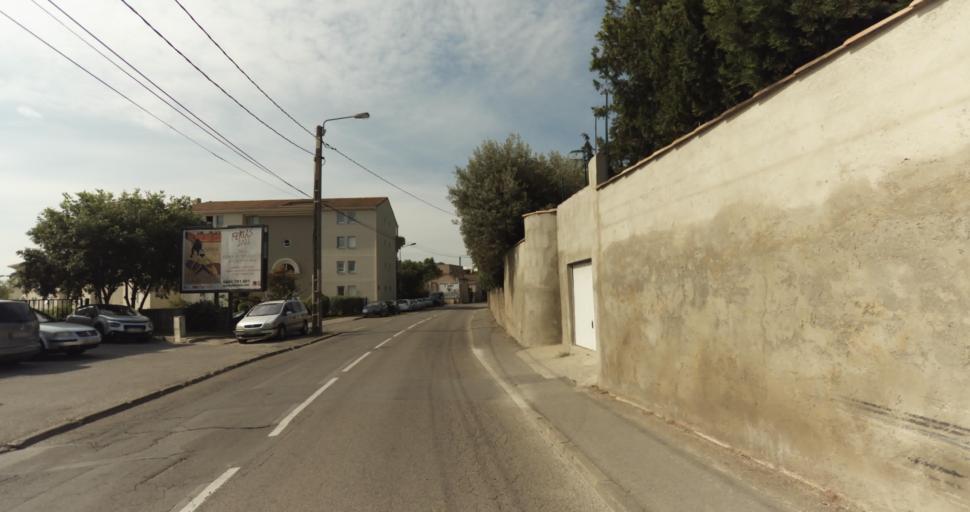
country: FR
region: Languedoc-Roussillon
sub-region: Departement du Gard
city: Rodilhan
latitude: 43.8525
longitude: 4.3973
